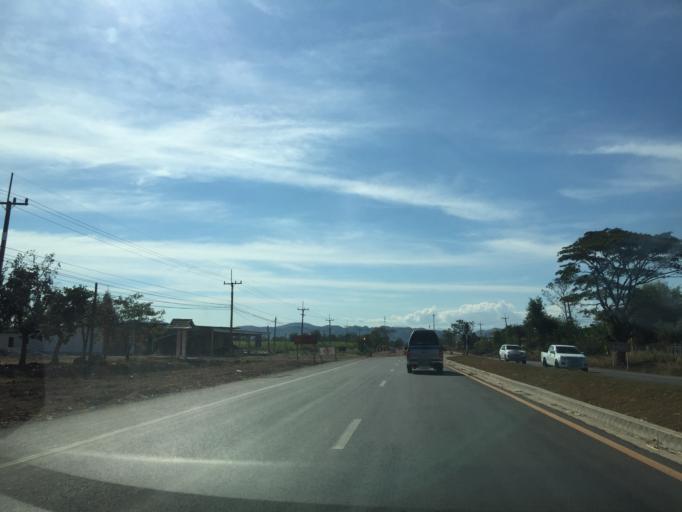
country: TH
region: Loei
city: Erawan
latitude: 17.3040
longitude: 101.8880
